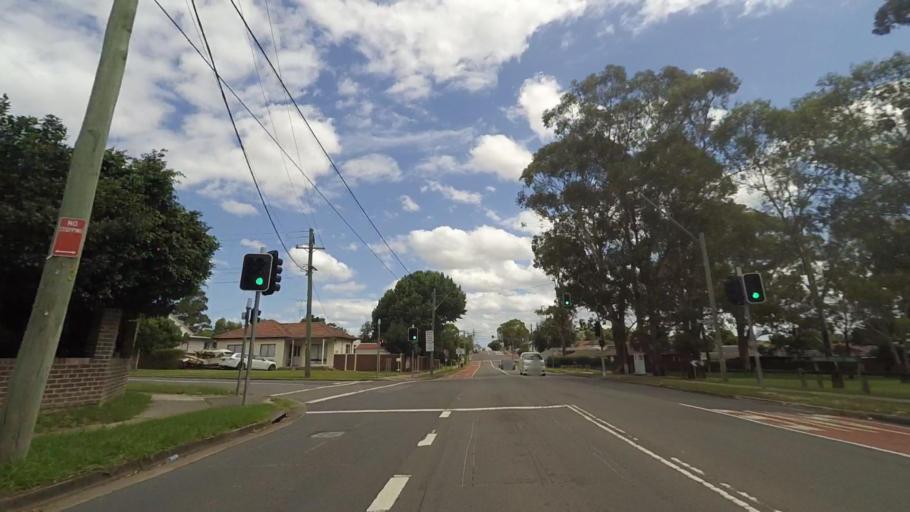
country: AU
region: New South Wales
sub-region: Holroyd
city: Guildford West
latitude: -33.8434
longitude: 150.9631
